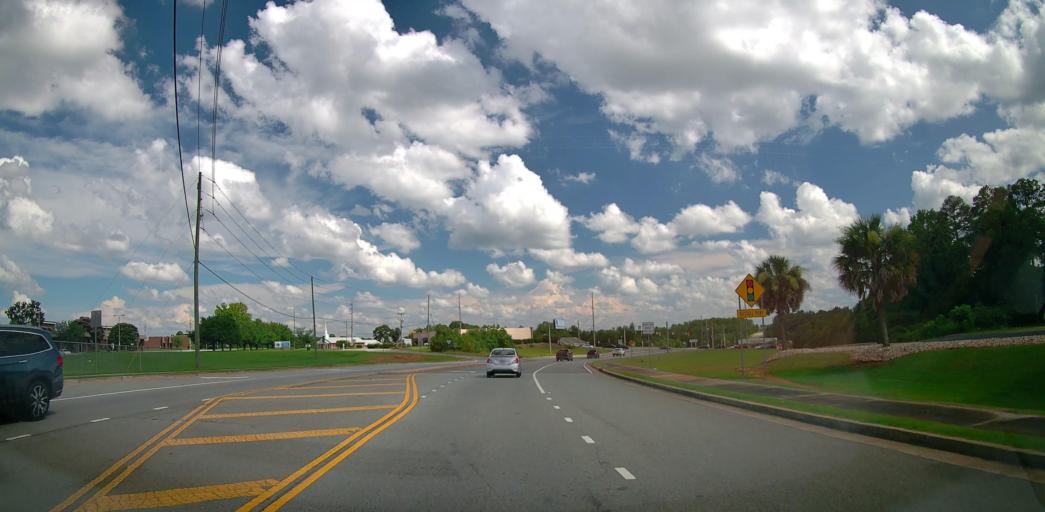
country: US
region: Georgia
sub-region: Houston County
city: Centerville
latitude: 32.5956
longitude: -83.6561
